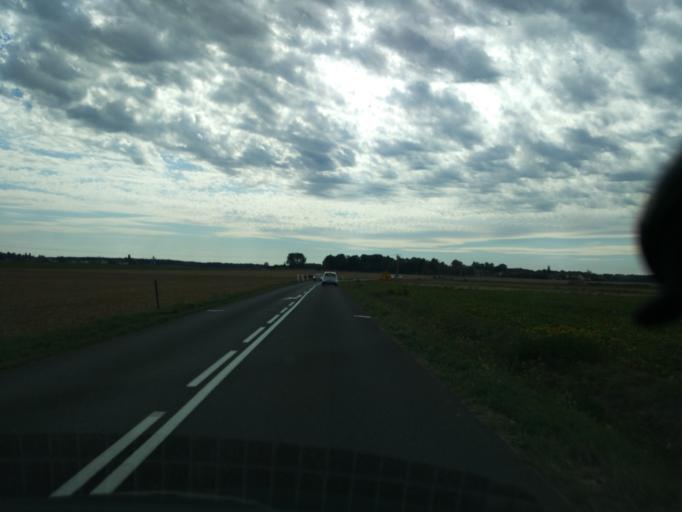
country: FR
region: Ile-de-France
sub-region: Departement de l'Essonne
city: Gometz-la-Ville
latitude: 48.6557
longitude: 2.1242
